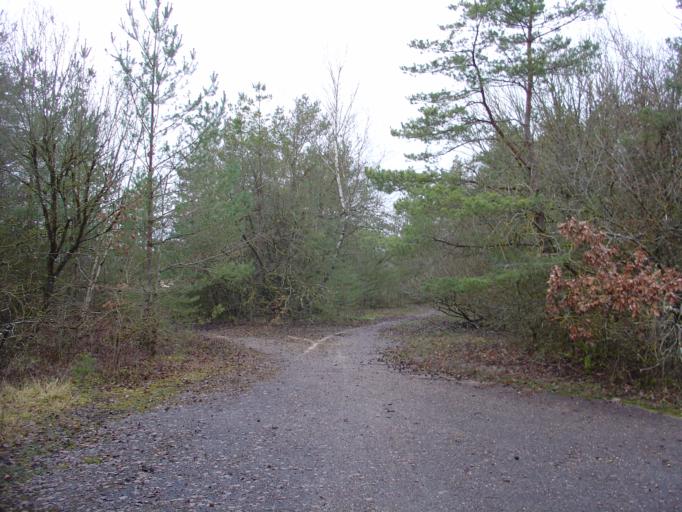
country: FR
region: Lorraine
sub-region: Departement de Meurthe-et-Moselle
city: Villey-Saint-Etienne
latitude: 48.7454
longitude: 5.9697
